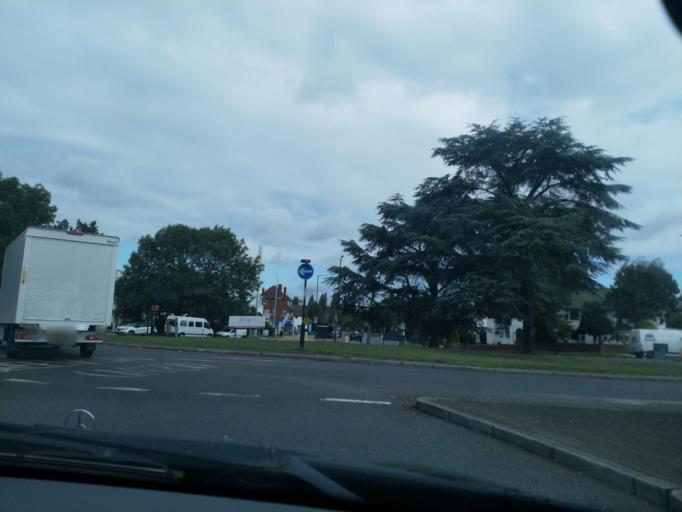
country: GB
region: England
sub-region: Greater London
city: Harrow on the Hill
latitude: 51.5667
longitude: -0.3213
